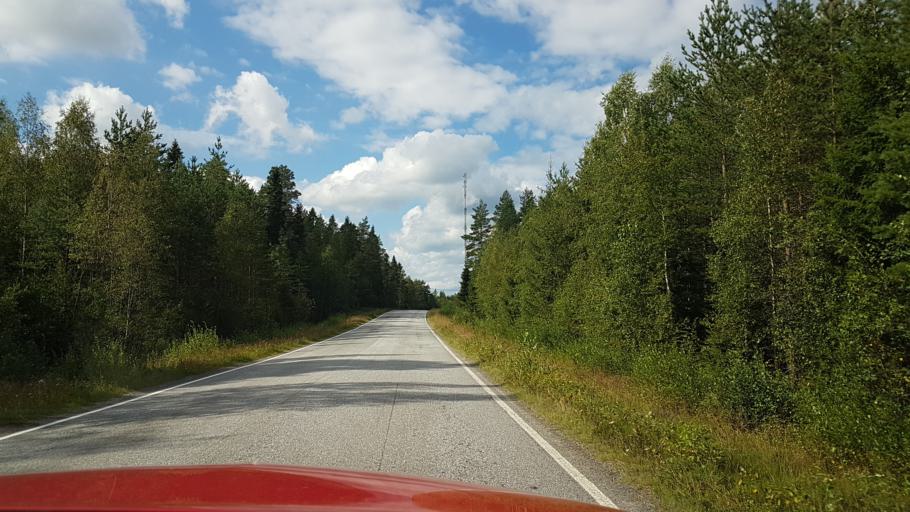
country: FI
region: Northern Ostrobothnia
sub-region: Ylivieska
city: Himanka
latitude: 64.0666
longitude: 23.6834
